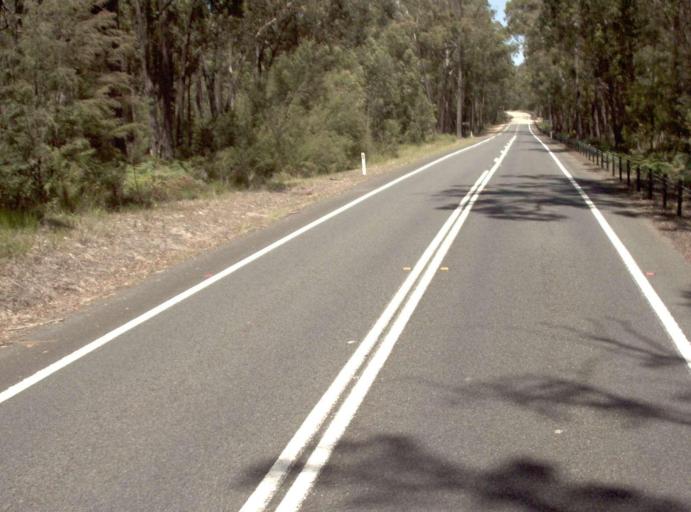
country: AU
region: Victoria
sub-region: East Gippsland
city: Lakes Entrance
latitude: -37.8154
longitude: 148.0289
